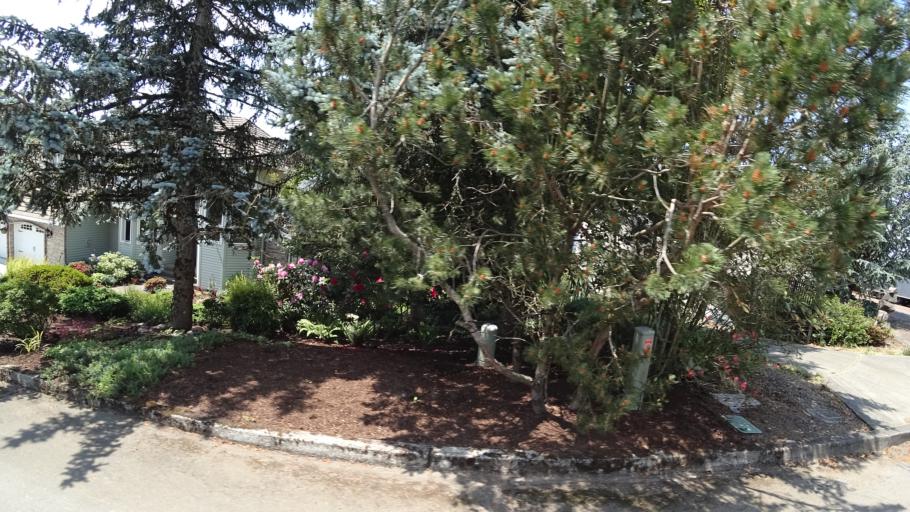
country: US
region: Oregon
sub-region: Clackamas County
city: Happy Valley
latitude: 45.4532
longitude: -122.5549
